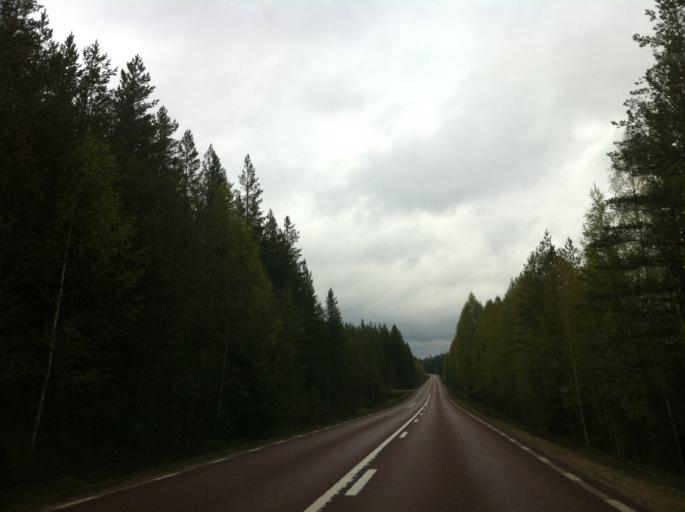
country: SE
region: Jaemtland
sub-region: Harjedalens Kommun
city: Sveg
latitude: 61.8800
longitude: 14.6281
